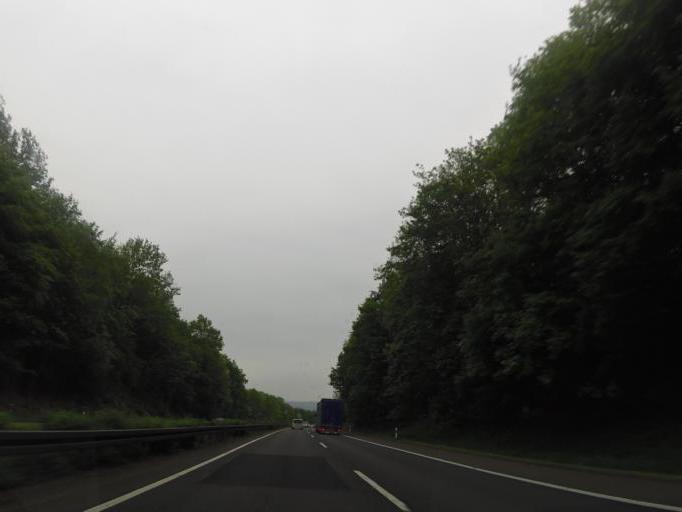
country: DE
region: Lower Saxony
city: Kalefeld
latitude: 51.8214
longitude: 10.1097
